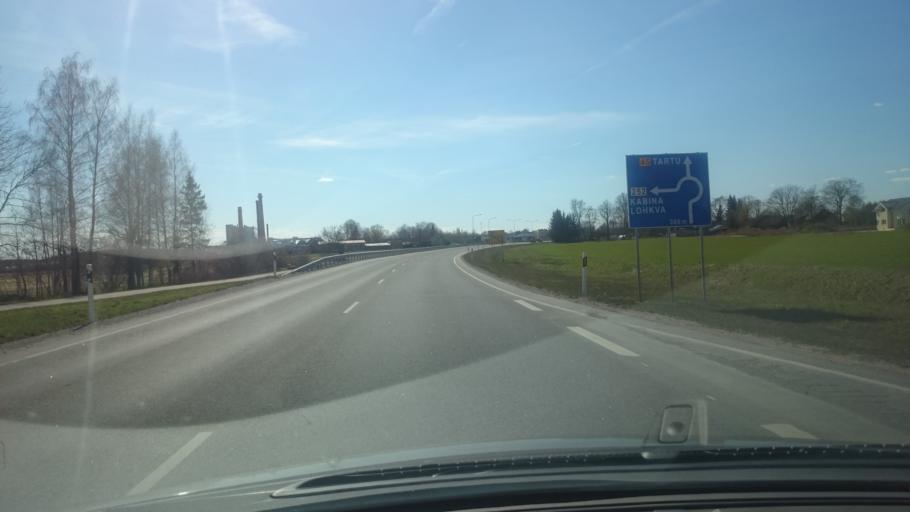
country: EE
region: Tartu
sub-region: Tartu linn
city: Tartu
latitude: 58.3723
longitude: 26.8057
